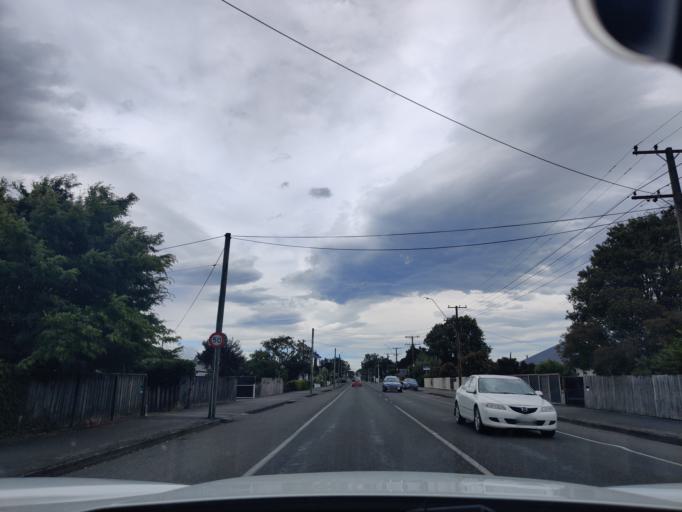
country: NZ
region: Wellington
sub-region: Masterton District
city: Masterton
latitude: -41.0321
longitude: 175.5206
